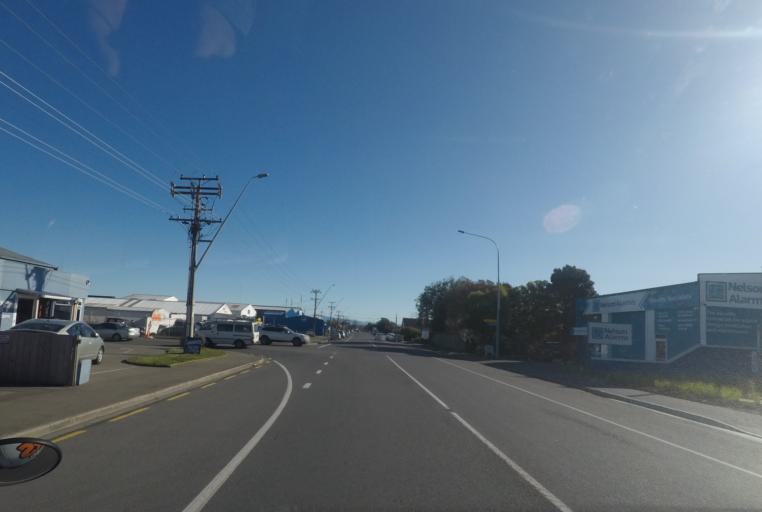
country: NZ
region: Nelson
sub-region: Nelson City
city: Nelson
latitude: -41.2908
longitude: 173.2430
